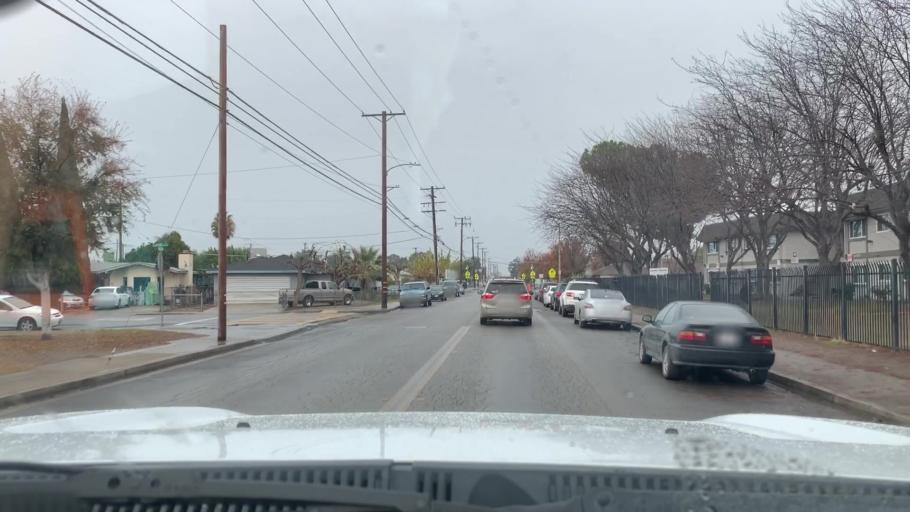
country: US
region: California
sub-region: Kern County
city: Delano
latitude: 35.7614
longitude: -119.2538
